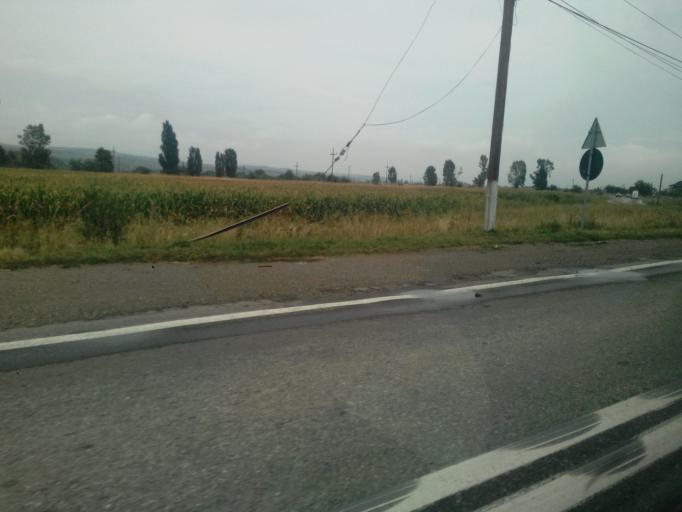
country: RO
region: Cluj
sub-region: Comuna Mihai Viteazu
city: Mihai Viteazu
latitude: 46.5261
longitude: 23.6995
